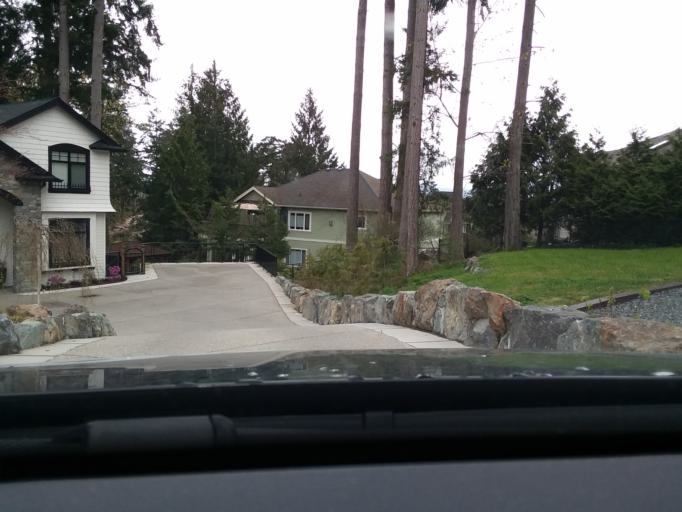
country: CA
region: British Columbia
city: North Saanich
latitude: 48.5516
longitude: -123.4016
